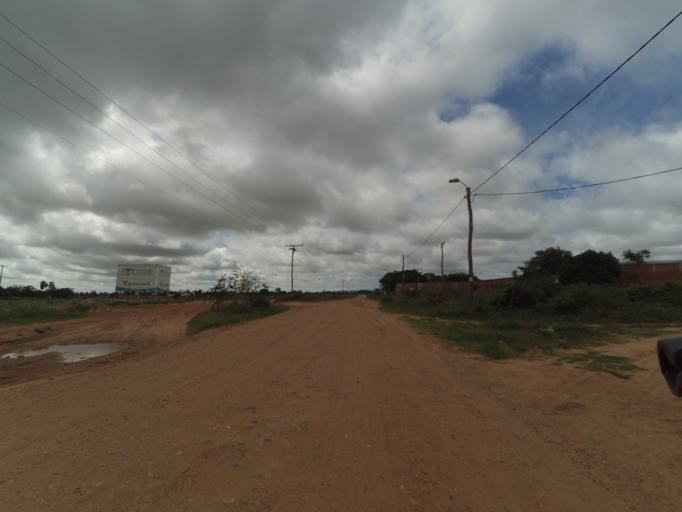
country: BO
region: Santa Cruz
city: Santa Rita
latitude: -17.8985
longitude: -63.2420
